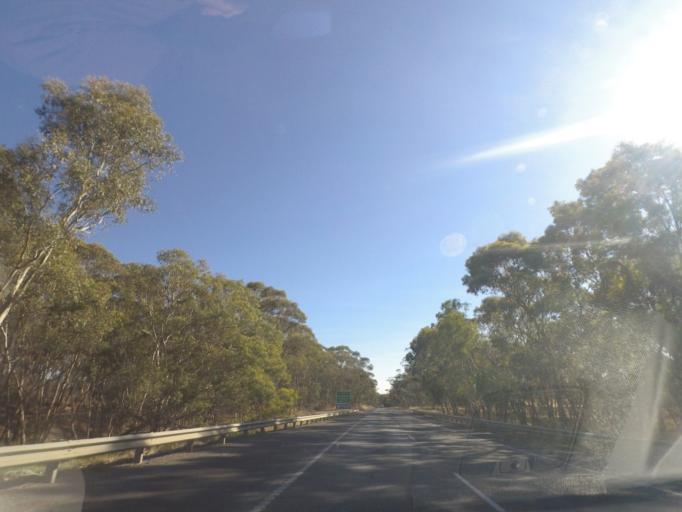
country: AU
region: Victoria
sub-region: Murrindindi
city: Kinglake West
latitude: -37.1734
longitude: 145.0745
